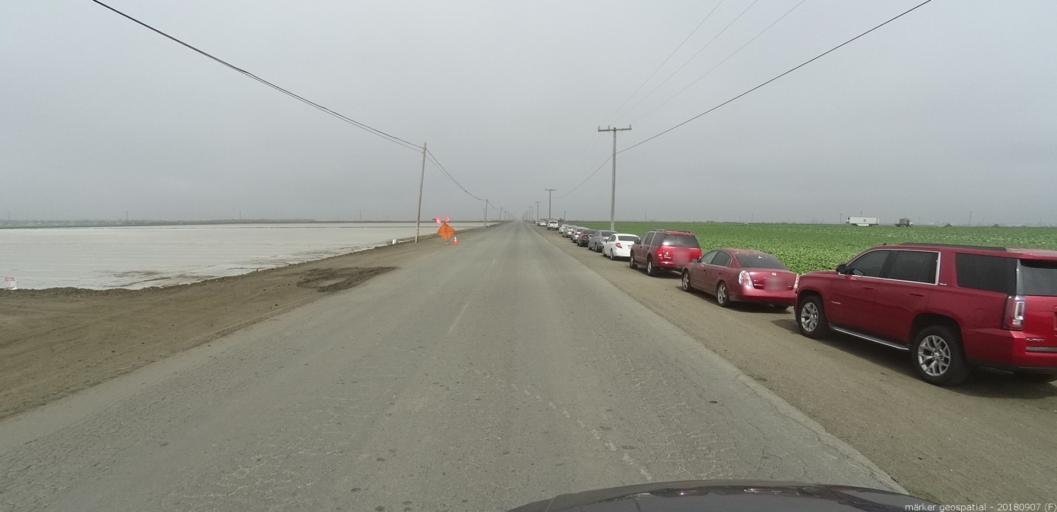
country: US
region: California
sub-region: Monterey County
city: Castroville
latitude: 36.7226
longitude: -121.7449
